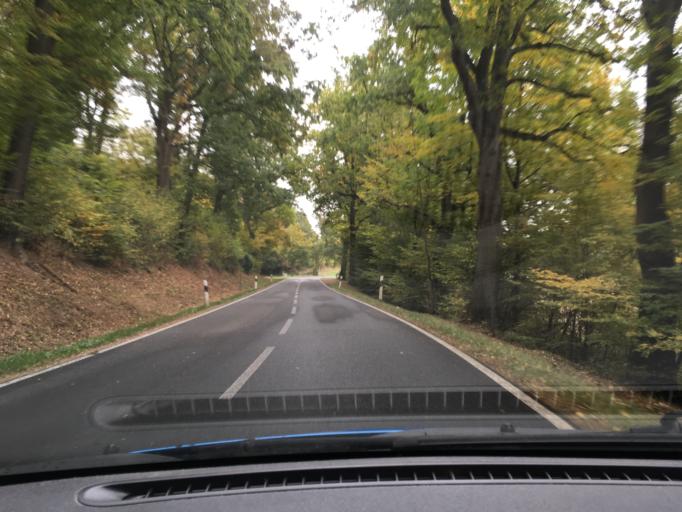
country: DE
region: Lower Saxony
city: Bodenfelde
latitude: 51.6285
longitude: 9.5818
